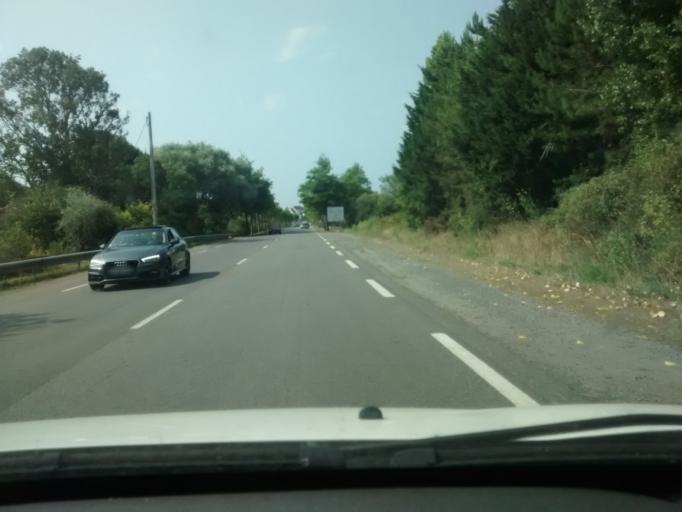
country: FR
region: Pays de la Loire
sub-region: Departement de la Loire-Atlantique
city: Pornichet
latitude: 47.2682
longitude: -2.3300
